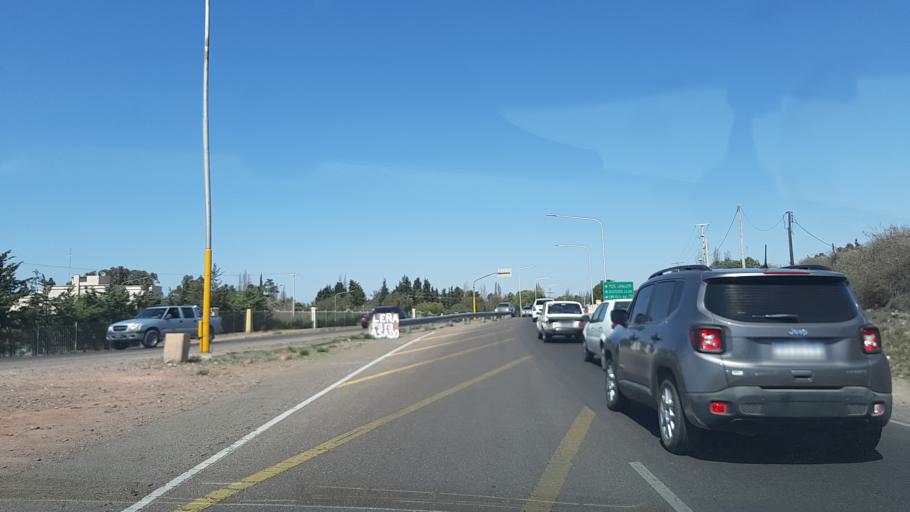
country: AR
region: Mendoza
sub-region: Departamento de Godoy Cruz
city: Godoy Cruz
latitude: -32.9716
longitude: -68.8816
